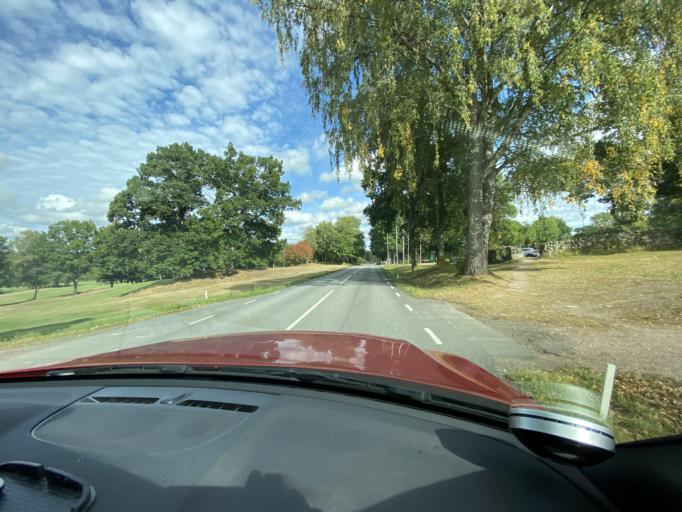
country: SE
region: Skane
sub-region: Hassleholms Kommun
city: Bjarnum
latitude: 56.3465
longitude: 13.7049
